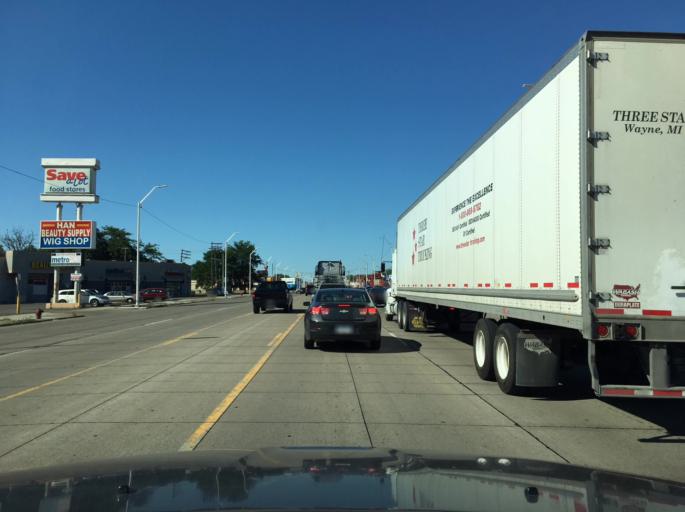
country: US
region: Michigan
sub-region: Wayne County
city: Detroit
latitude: 42.3630
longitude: -83.0251
